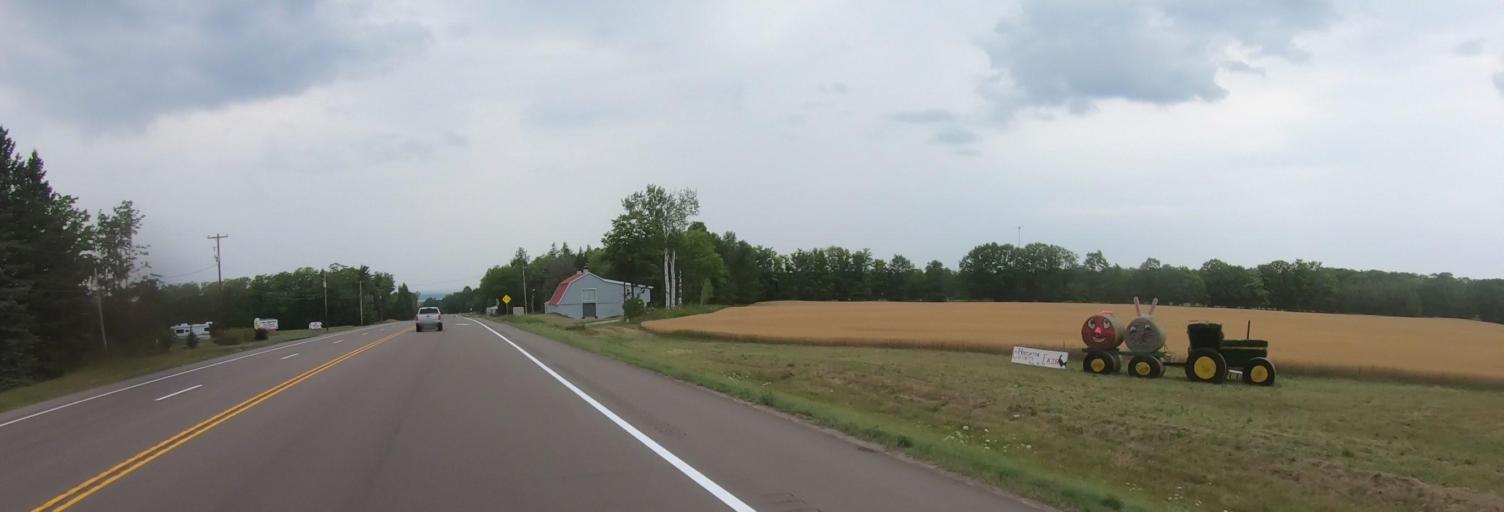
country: US
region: Michigan
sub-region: Houghton County
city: Dollar Bay
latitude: 46.9872
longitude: -88.4723
